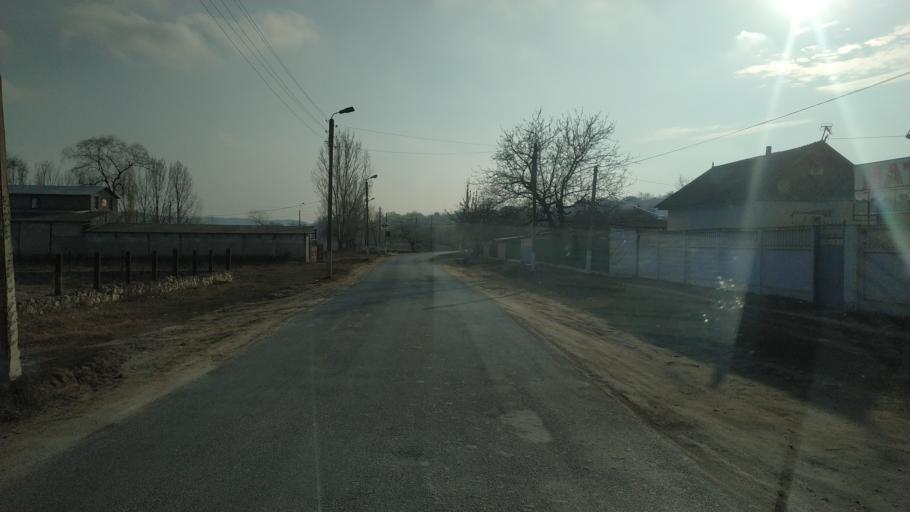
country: MD
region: Hincesti
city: Dancu
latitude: 46.7776
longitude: 28.3477
